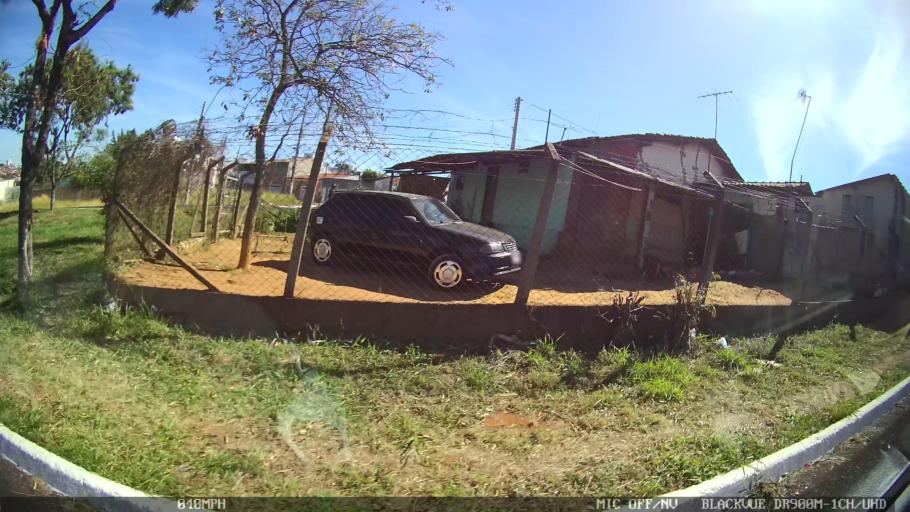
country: BR
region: Sao Paulo
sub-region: Franca
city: Franca
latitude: -20.5278
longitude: -47.3707
